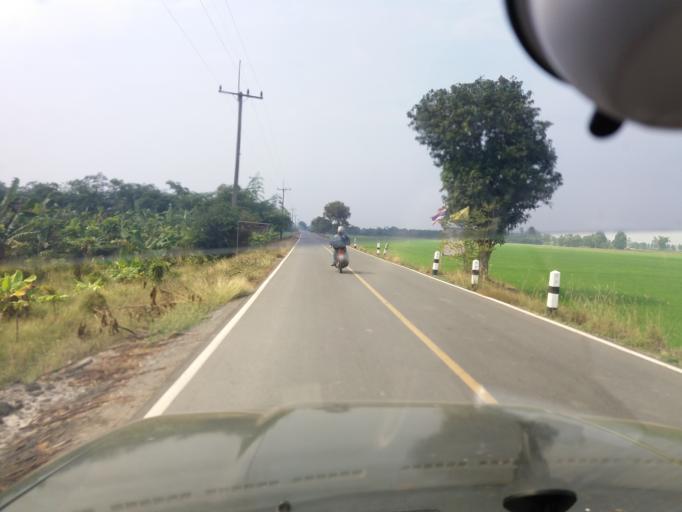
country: TH
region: Suphan Buri
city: Doem Bang Nang Buat
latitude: 14.8920
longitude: 100.1624
